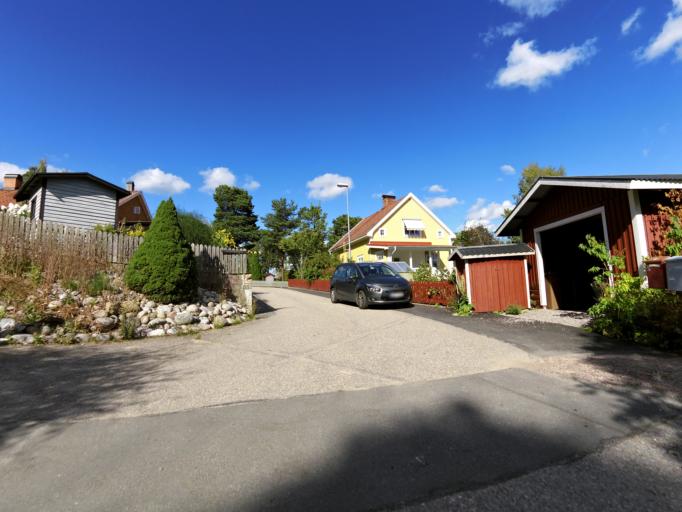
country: SE
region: Gaevleborg
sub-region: Gavle Kommun
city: Gavle
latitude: 60.6964
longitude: 17.1520
